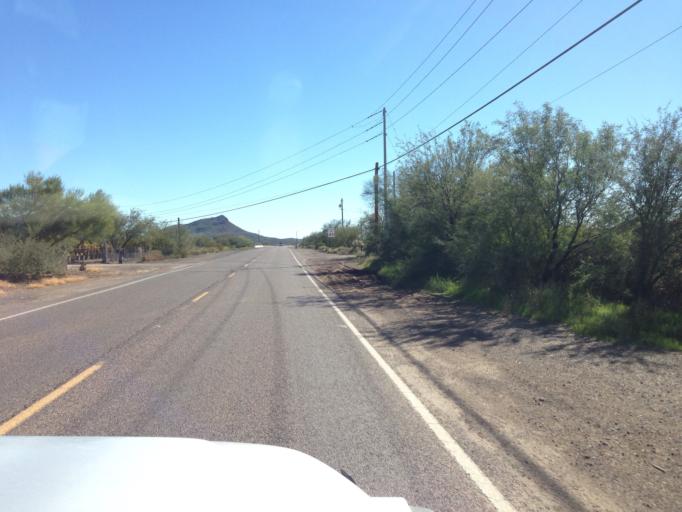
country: US
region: Arizona
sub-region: Maricopa County
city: New River
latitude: 33.9102
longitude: -112.0858
